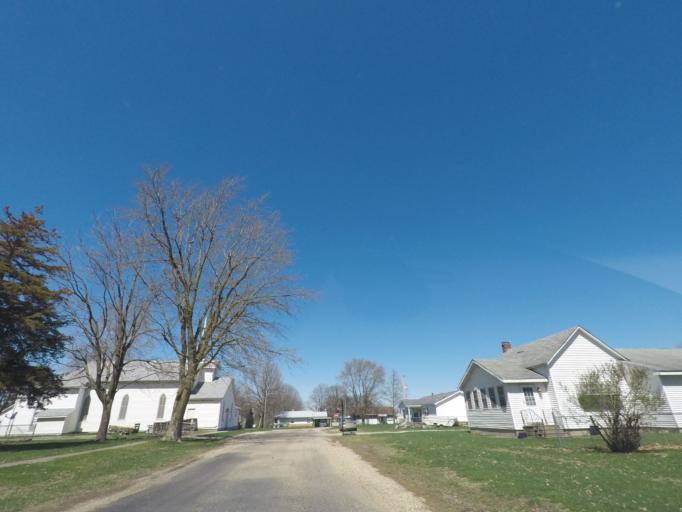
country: US
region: Illinois
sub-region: Macon County
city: Warrensburg
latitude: 39.9676
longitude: -89.1616
